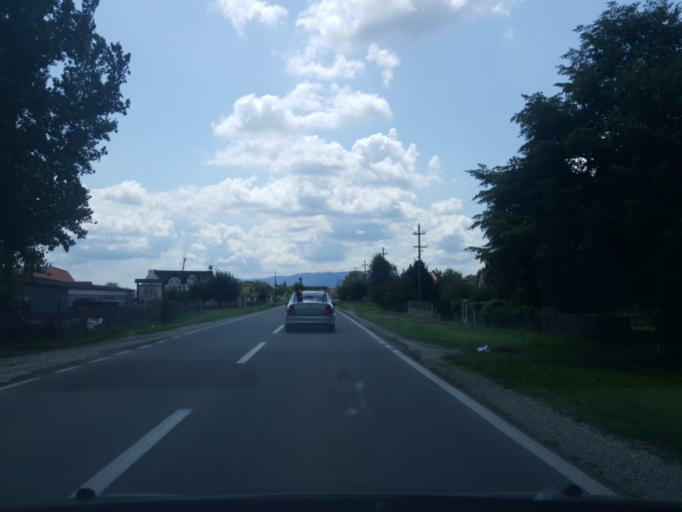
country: RS
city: Kozjak
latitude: 44.6246
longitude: 19.2696
